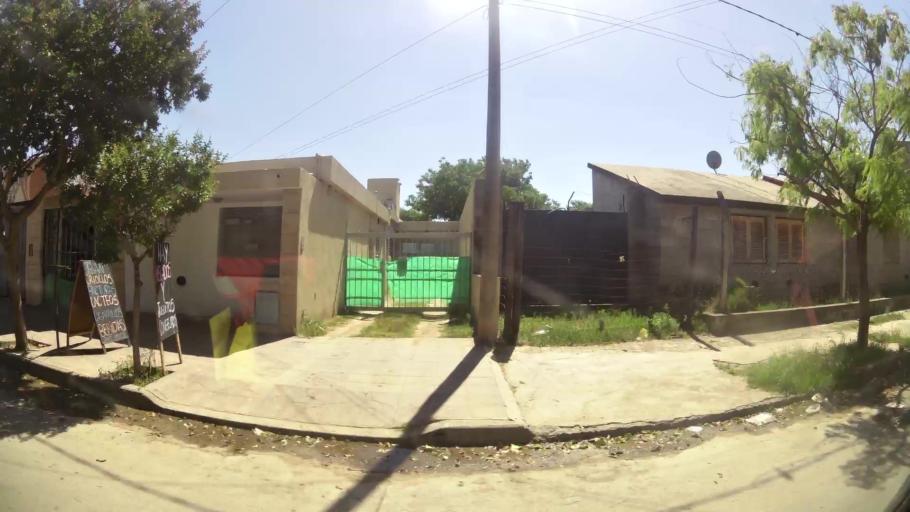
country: AR
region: Cordoba
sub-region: Departamento de Capital
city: Cordoba
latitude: -31.3702
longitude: -64.1430
